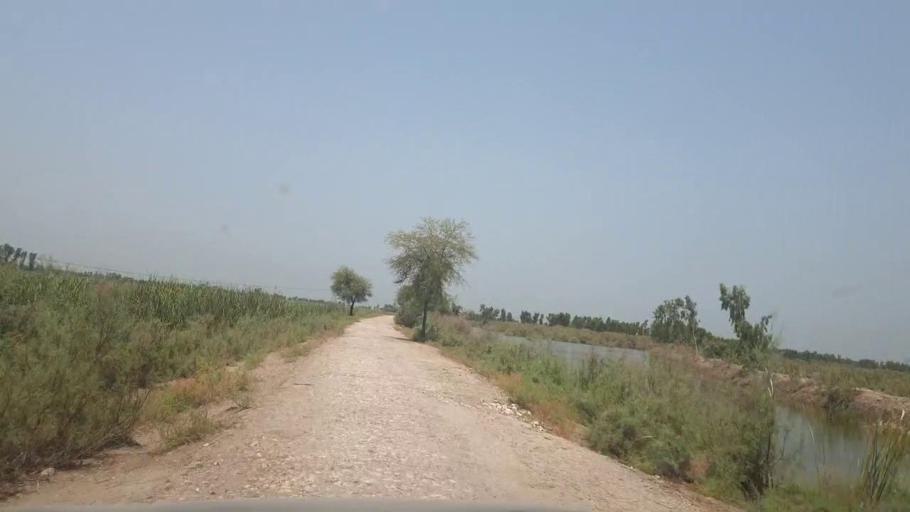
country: PK
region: Sindh
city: Lakhi
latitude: 27.8557
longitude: 68.6249
